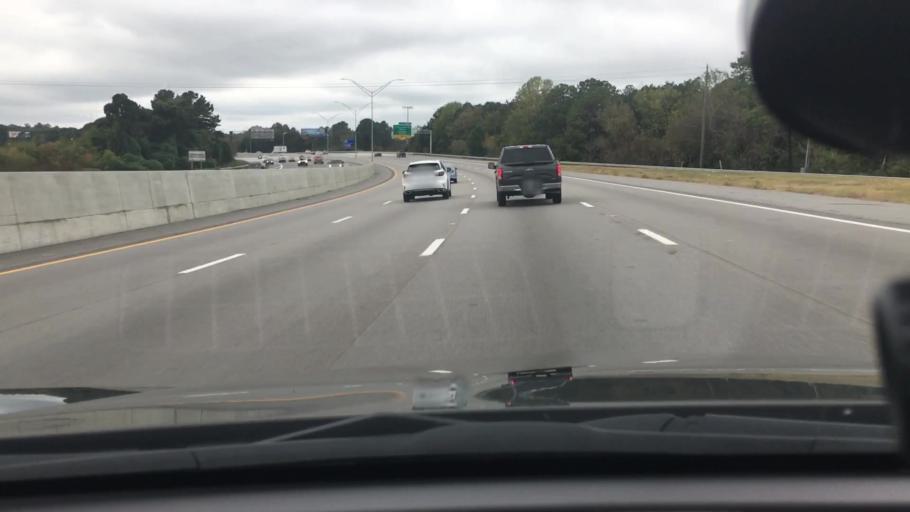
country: US
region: North Carolina
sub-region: Wake County
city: Raleigh
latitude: 35.7544
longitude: -78.6378
